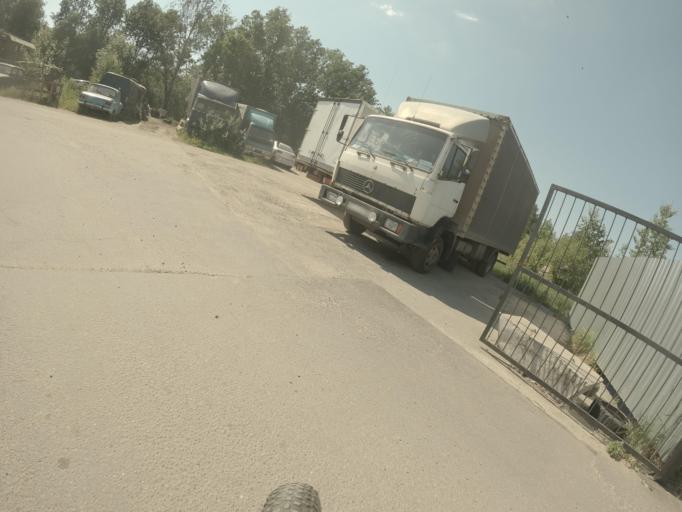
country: RU
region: St.-Petersburg
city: Obukhovo
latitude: 59.8412
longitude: 30.4672
